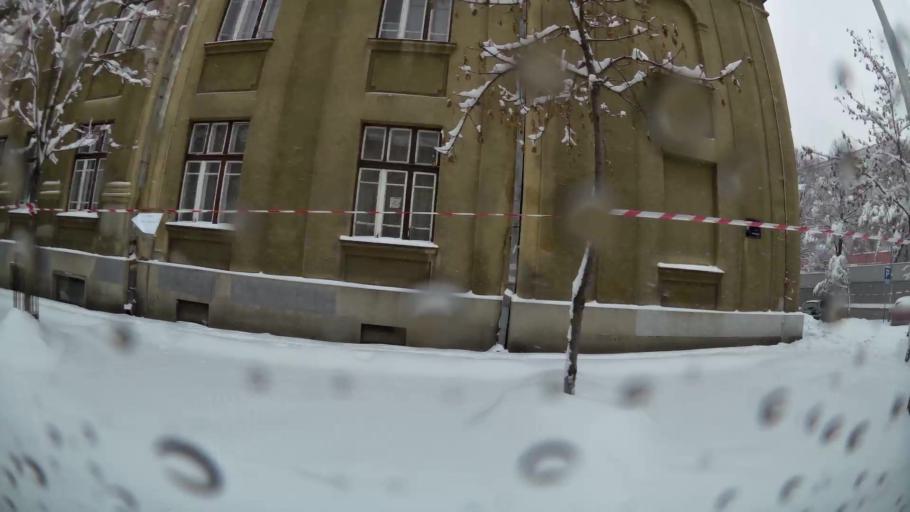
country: RS
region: Central Serbia
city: Belgrade
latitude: 44.8001
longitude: 20.4612
